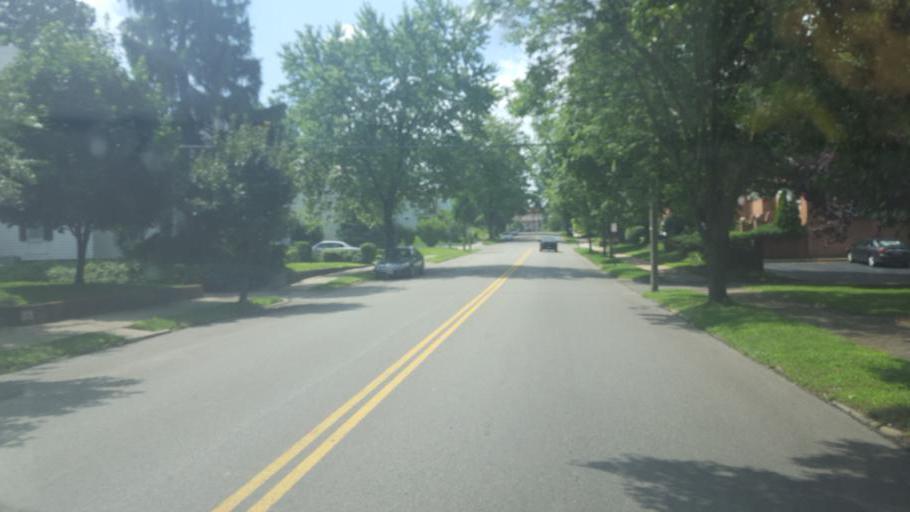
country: US
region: Ohio
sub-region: Fairfield County
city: Lancaster
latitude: 39.7182
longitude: -82.5988
